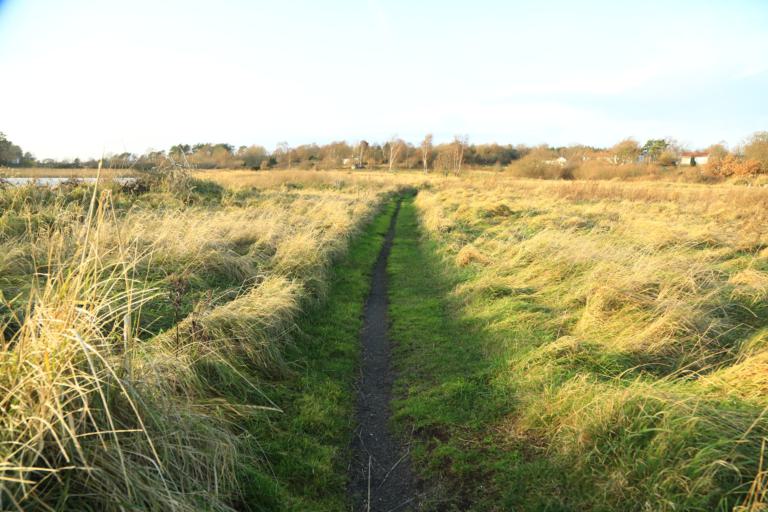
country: SE
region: Halland
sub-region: Varbergs Kommun
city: Varberg
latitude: 57.1905
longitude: 12.2036
